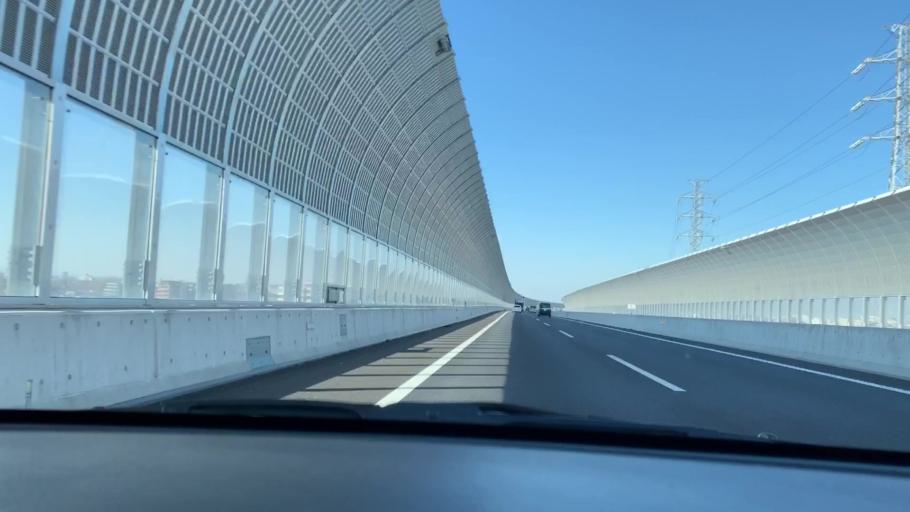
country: JP
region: Chiba
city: Matsudo
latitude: 35.7804
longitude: 139.8853
